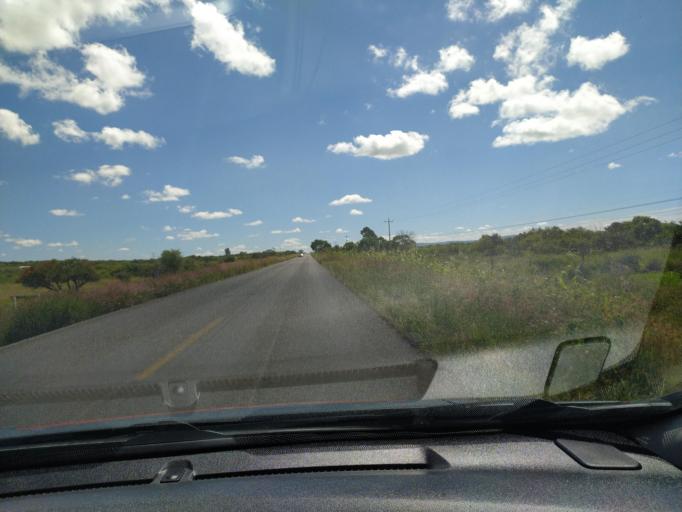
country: MX
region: Jalisco
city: Valle de Guadalupe
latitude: 21.0218
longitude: -102.5380
